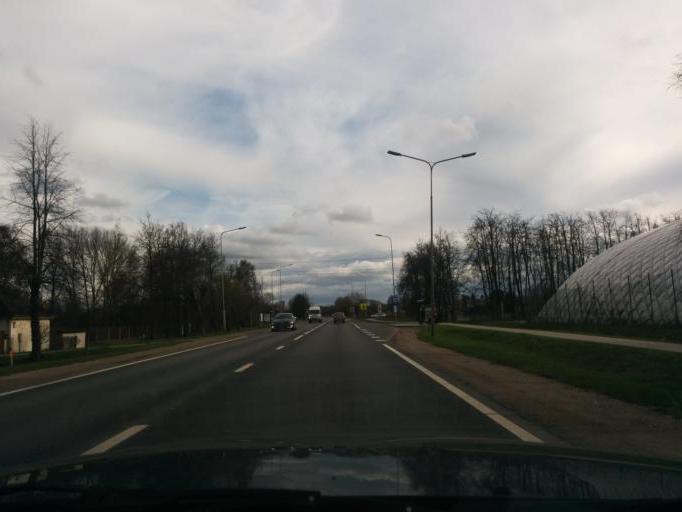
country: LV
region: Jelgava
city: Jelgava
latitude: 56.6269
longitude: 23.7253
